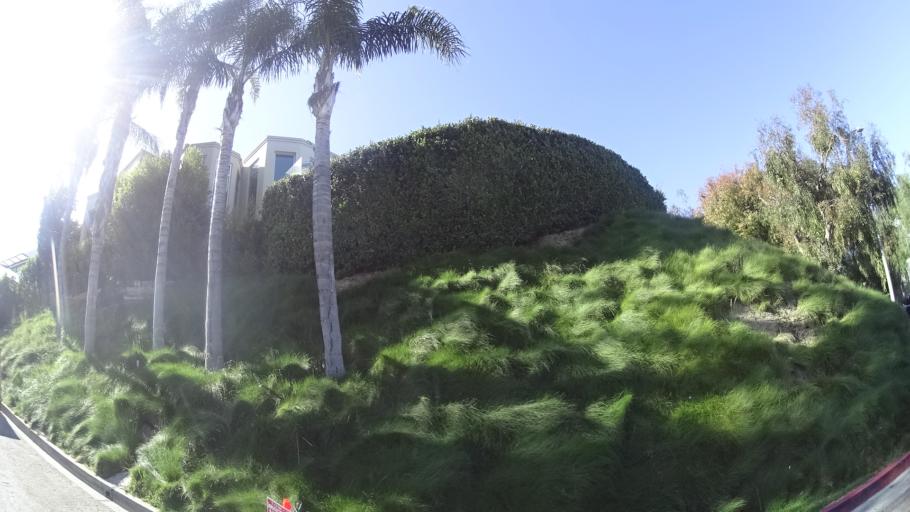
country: US
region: California
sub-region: Los Angeles County
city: West Hollywood
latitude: 34.0977
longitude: -118.3863
